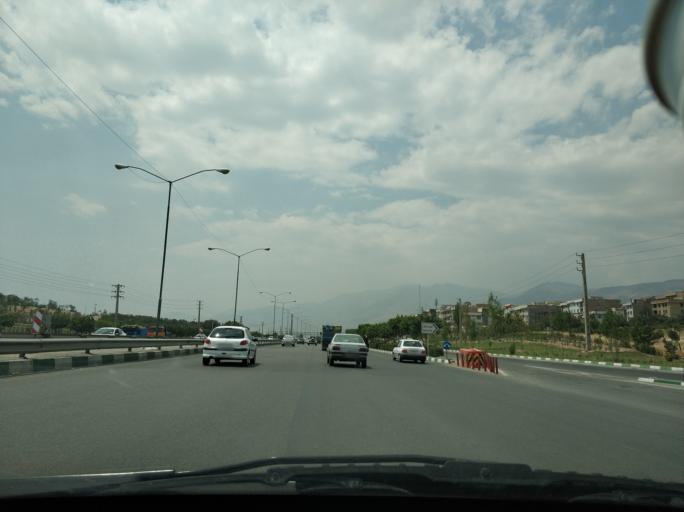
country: IR
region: Tehran
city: Tajrish
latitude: 35.7649
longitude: 51.5657
